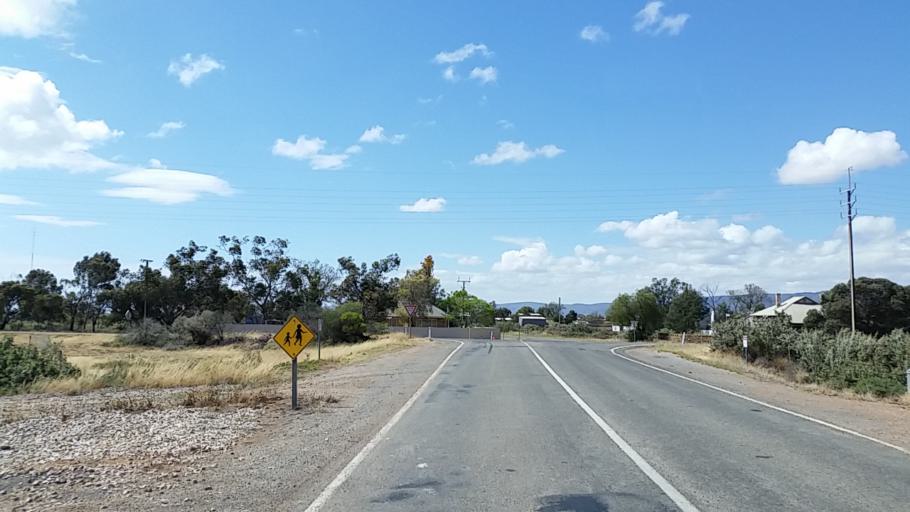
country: AU
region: South Australia
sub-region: Port Pirie City and Dists
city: Solomontown
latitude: -33.1940
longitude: 138.0433
